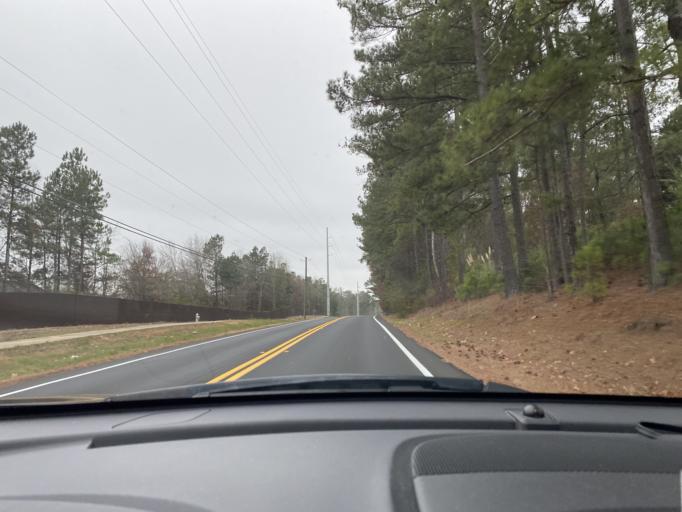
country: US
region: Georgia
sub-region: Gwinnett County
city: Grayson
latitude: 33.9144
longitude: -83.9292
